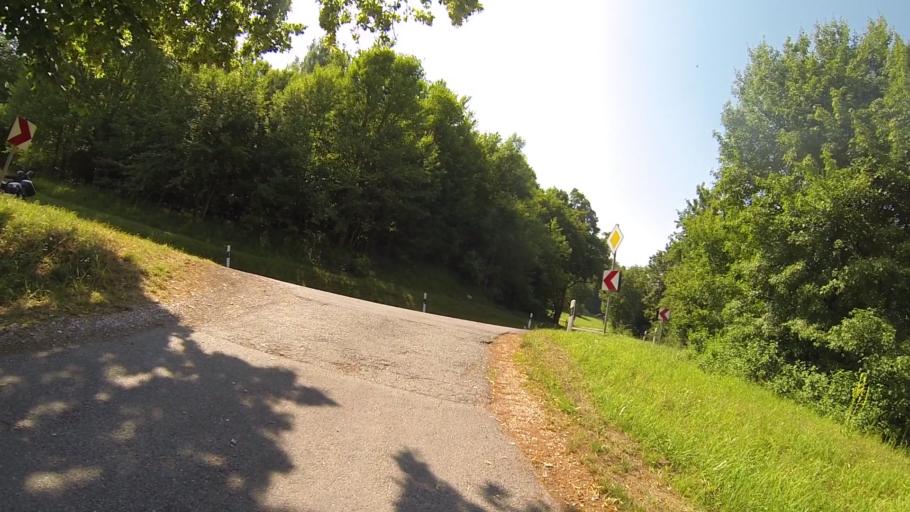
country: DE
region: Baden-Wuerttemberg
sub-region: Regierungsbezirk Stuttgart
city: Konigsbronn
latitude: 48.7428
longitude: 10.1026
